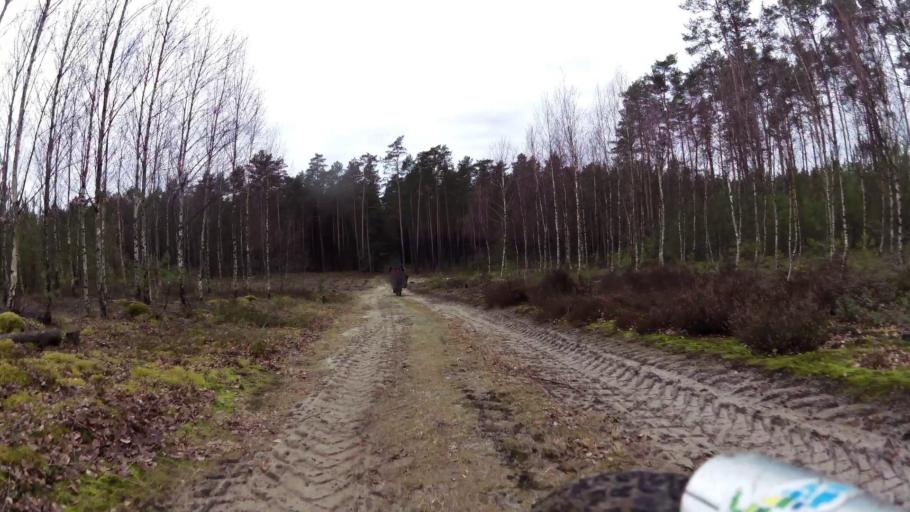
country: PL
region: Pomeranian Voivodeship
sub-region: Powiat bytowski
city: Kolczyglowy
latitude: 54.2385
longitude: 17.2623
